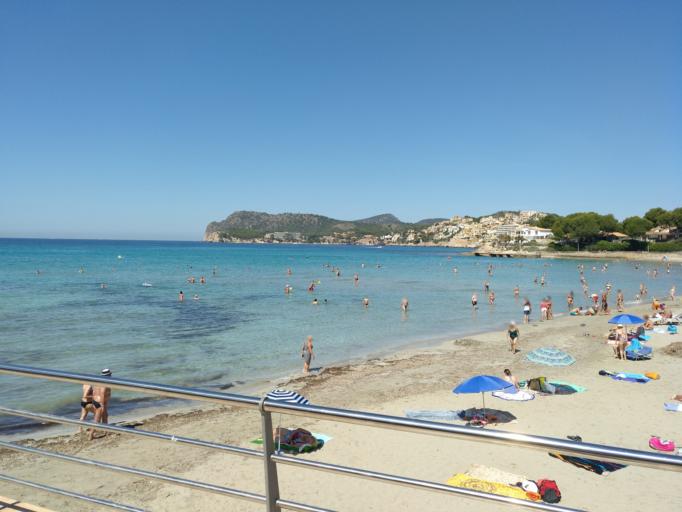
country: ES
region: Balearic Islands
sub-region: Illes Balears
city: Santa Ponsa
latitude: 39.5342
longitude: 2.4576
